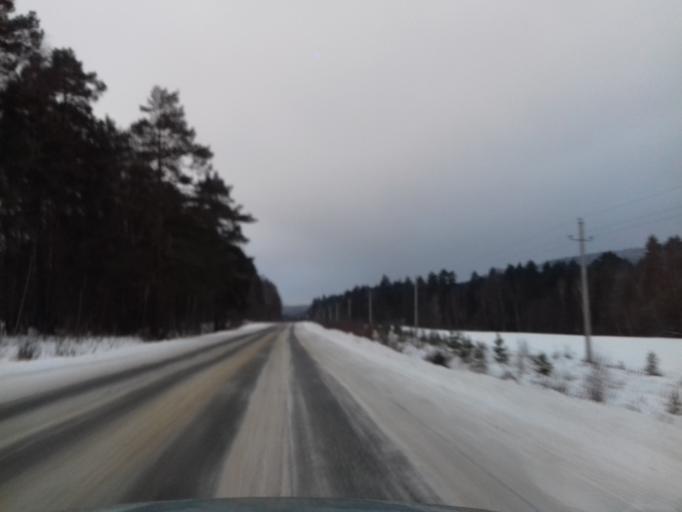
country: RU
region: Bashkortostan
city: Verkhniy Avzyan
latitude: 53.6201
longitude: 57.7519
